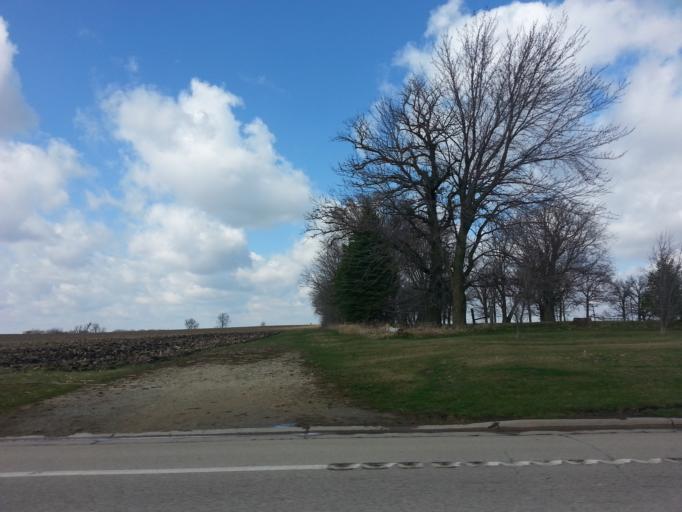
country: US
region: Minnesota
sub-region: Dodge County
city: Mantorville
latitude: 44.0803
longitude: -92.8102
